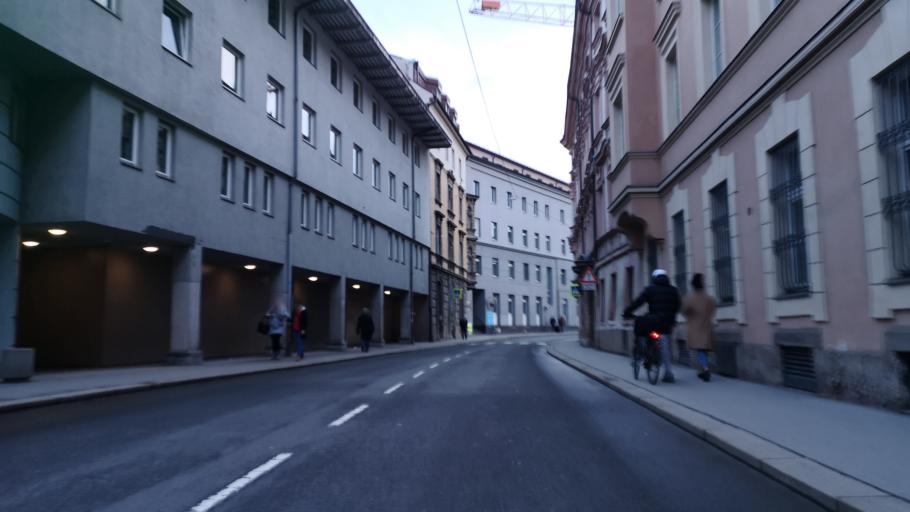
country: AT
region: Tyrol
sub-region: Innsbruck Stadt
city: Innsbruck
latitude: 47.2685
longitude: 11.3994
